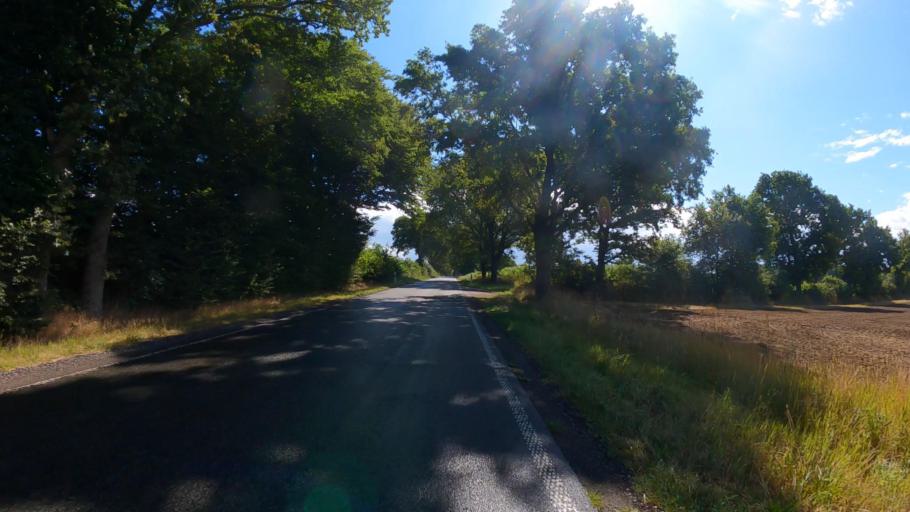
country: DE
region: Schleswig-Holstein
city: Armstedt
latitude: 53.9607
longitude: 9.8594
